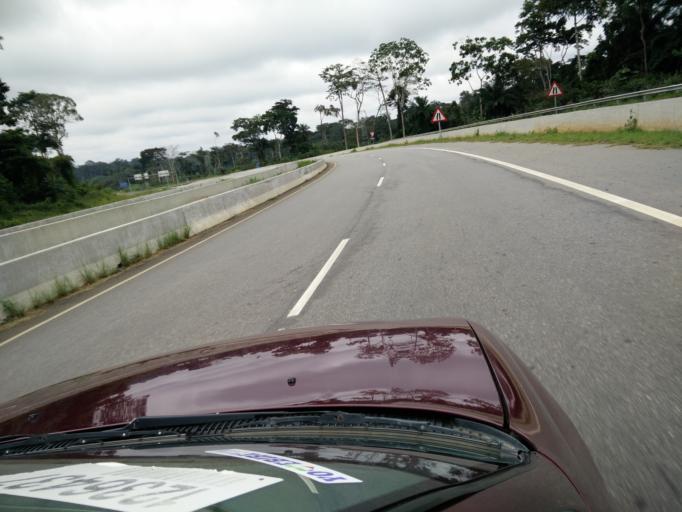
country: GQ
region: Wele-Nzas
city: Anisoc
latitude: 1.6708
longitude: 10.9916
